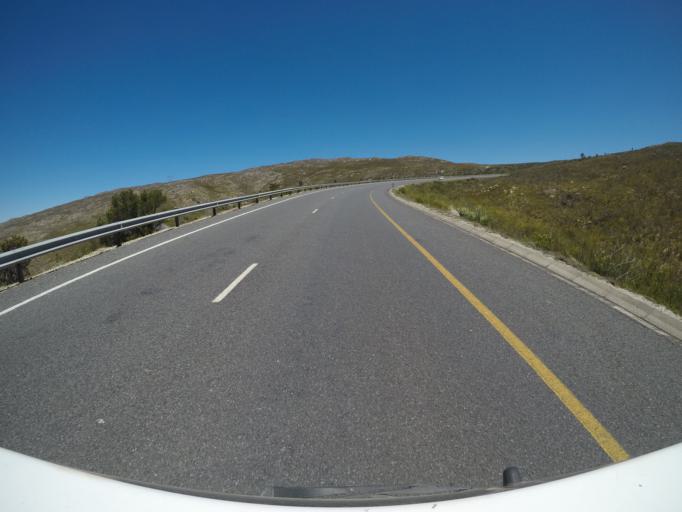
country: ZA
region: Western Cape
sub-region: Overberg District Municipality
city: Grabouw
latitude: -34.2214
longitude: 19.1767
